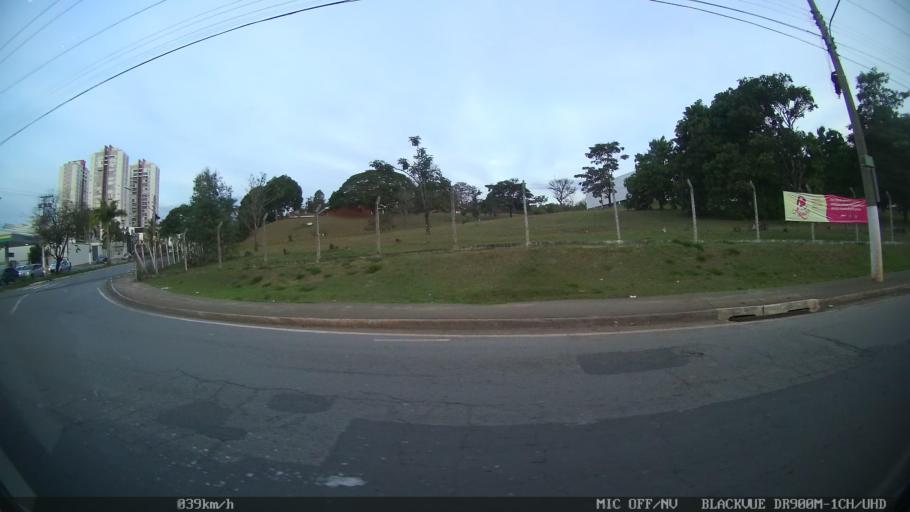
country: BR
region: Sao Paulo
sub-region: Limeira
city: Limeira
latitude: -22.5457
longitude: -47.4221
